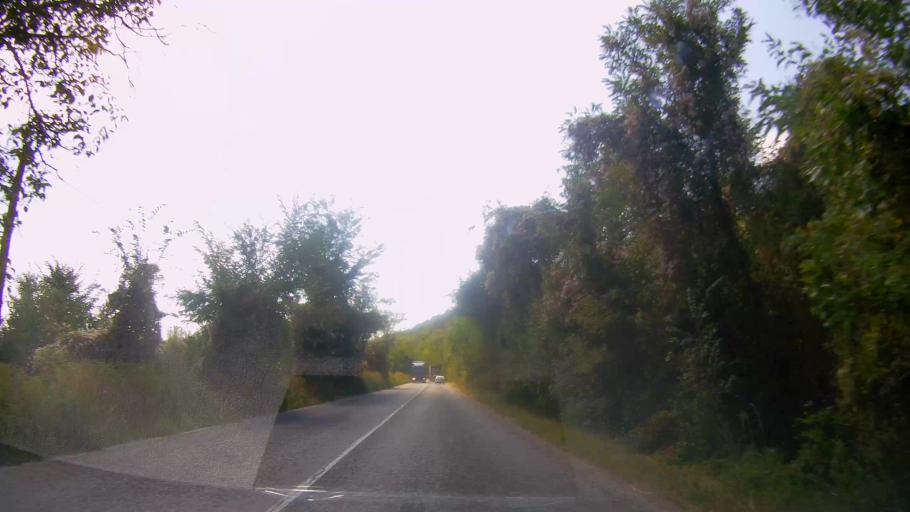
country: BG
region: Veliko Turnovo
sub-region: Obshtina Polski Trumbesh
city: Polski Trumbesh
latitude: 43.4385
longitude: 25.6542
